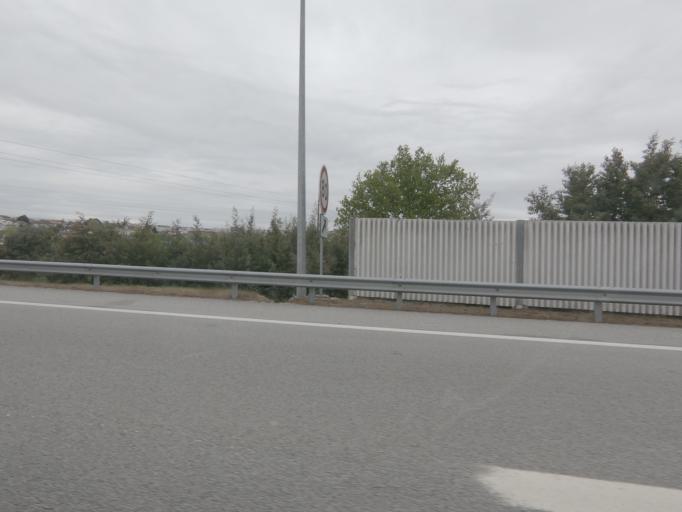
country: PT
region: Viseu
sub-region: Mangualde
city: Mangualde
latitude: 40.6188
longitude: -7.7622
